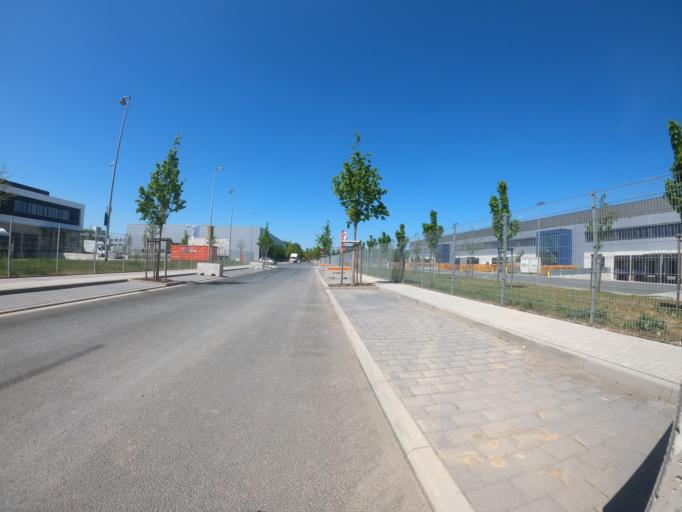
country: DE
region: Hesse
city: Raunheim
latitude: 50.0382
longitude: 8.4826
